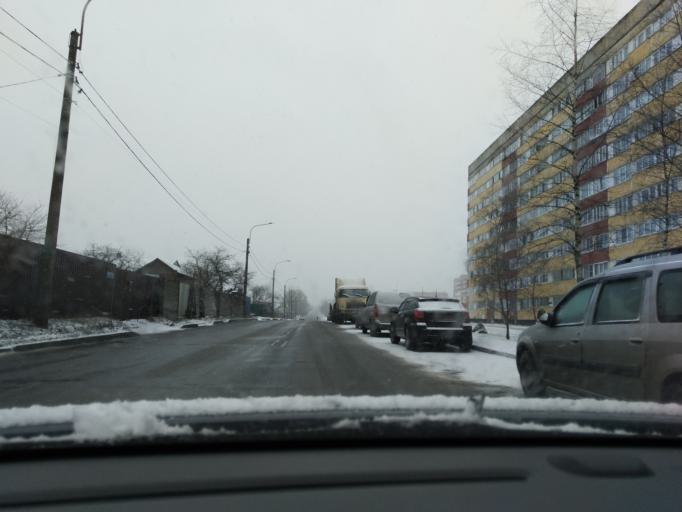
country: RU
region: St.-Petersburg
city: Krasnoye Selo
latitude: 59.7472
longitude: 30.0915
